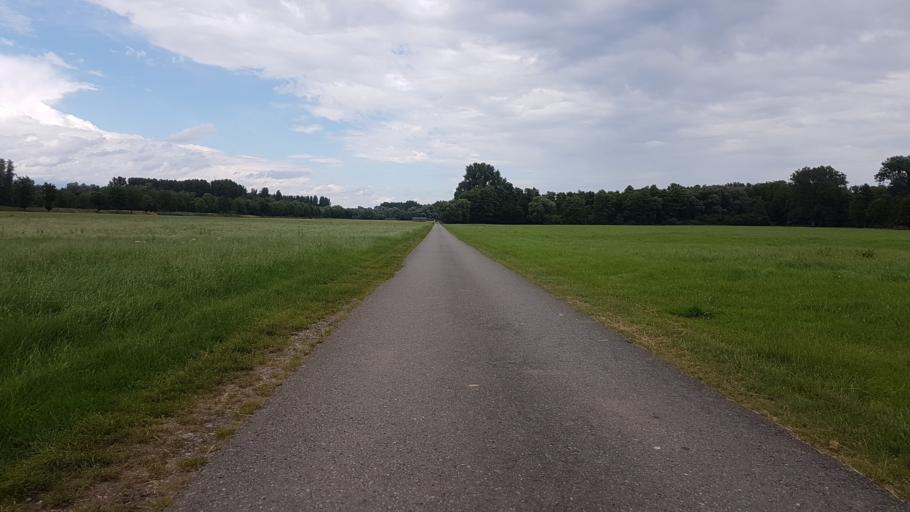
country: DE
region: Baden-Wuerttemberg
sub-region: Tuebingen Region
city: Neufra
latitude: 48.1253
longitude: 9.4591
